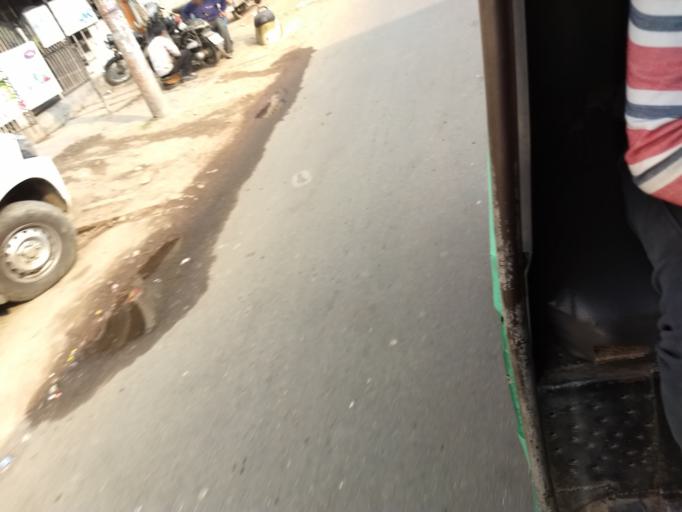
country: IN
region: Uttar Pradesh
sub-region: Kanpur
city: Kanpur
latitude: 26.4488
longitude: 80.3197
